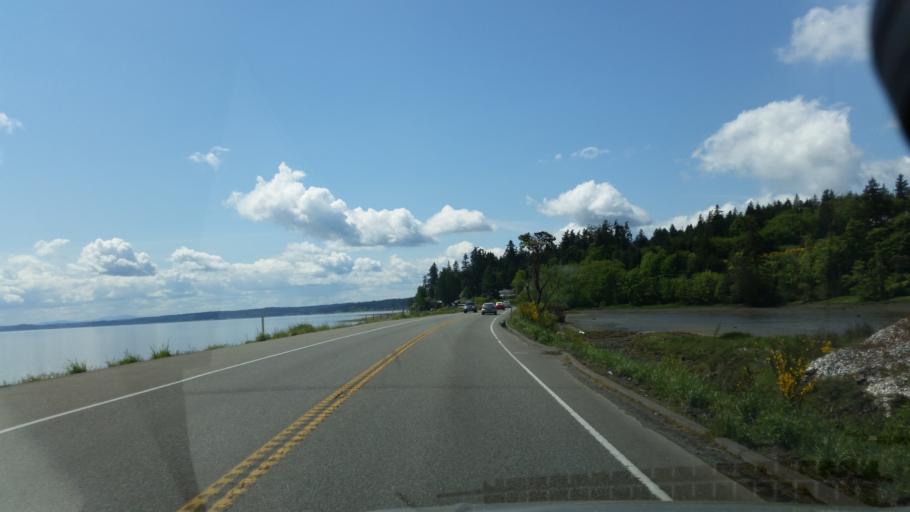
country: US
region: Washington
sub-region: Pierce County
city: Wauna
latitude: 47.3812
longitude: -122.6364
